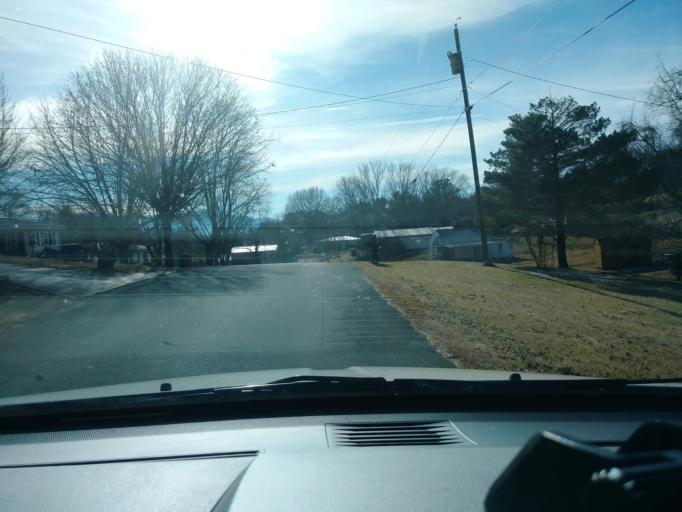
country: US
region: Tennessee
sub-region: Greene County
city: Greeneville
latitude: 36.1257
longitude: -82.8651
